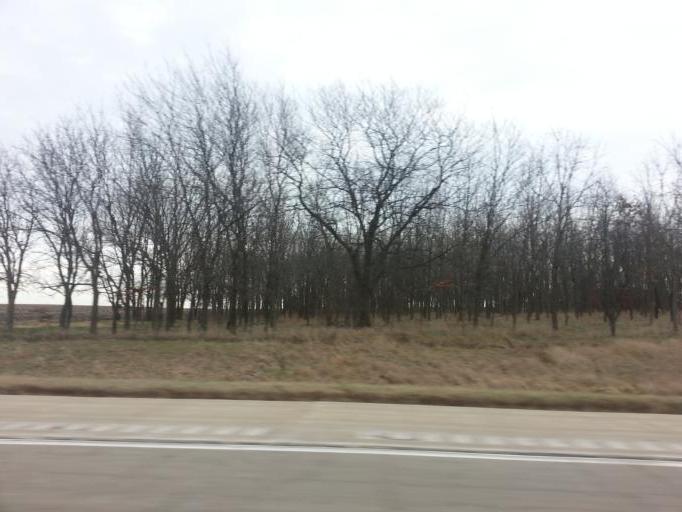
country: US
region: Illinois
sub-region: Woodford County
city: El Paso
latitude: 40.7657
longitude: -89.0345
